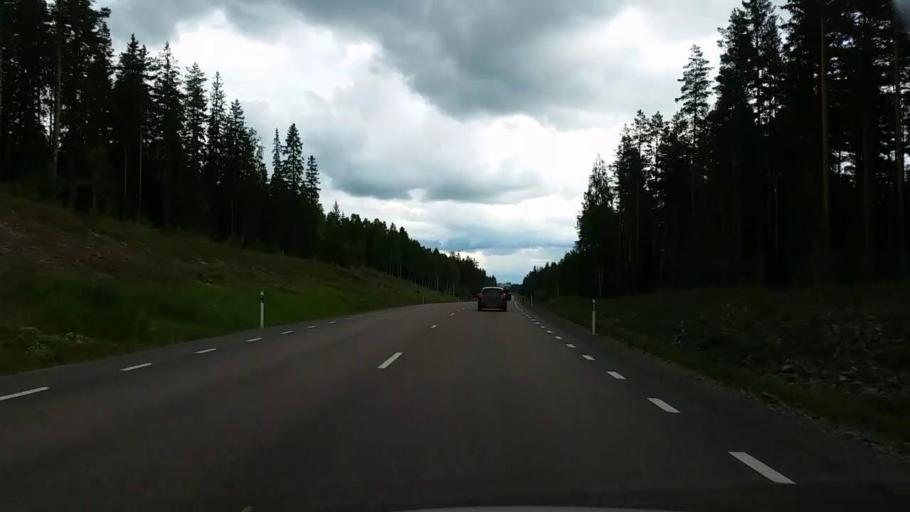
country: SE
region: Dalarna
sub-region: Avesta Kommun
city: Horndal
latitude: 60.4546
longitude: 16.4448
